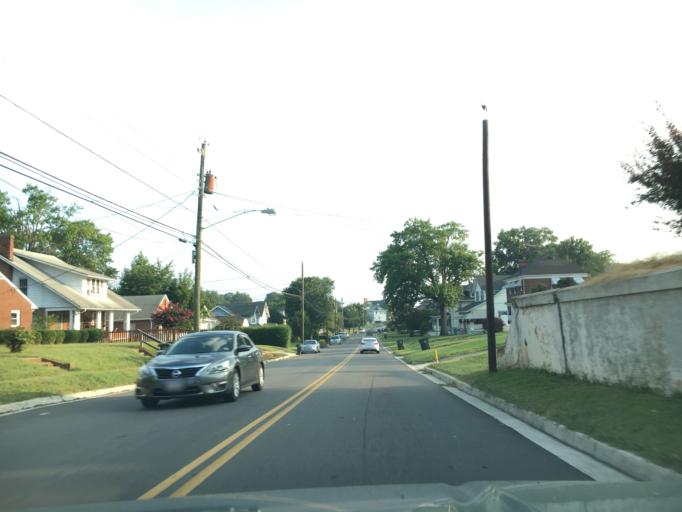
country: US
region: Virginia
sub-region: City of Lynchburg
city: West Lynchburg
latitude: 37.3929
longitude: -79.1721
